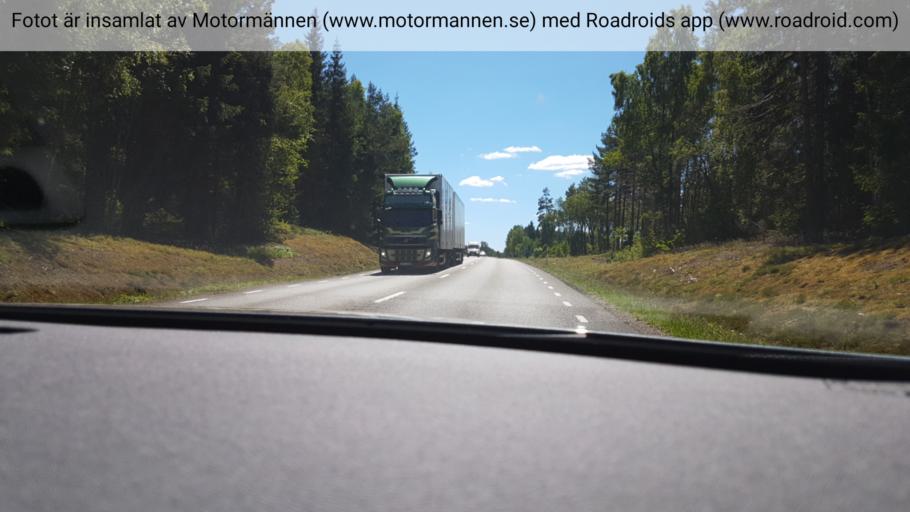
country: SE
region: Joenkoeping
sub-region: Jonkopings Kommun
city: Taberg
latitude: 57.6739
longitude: 13.8415
